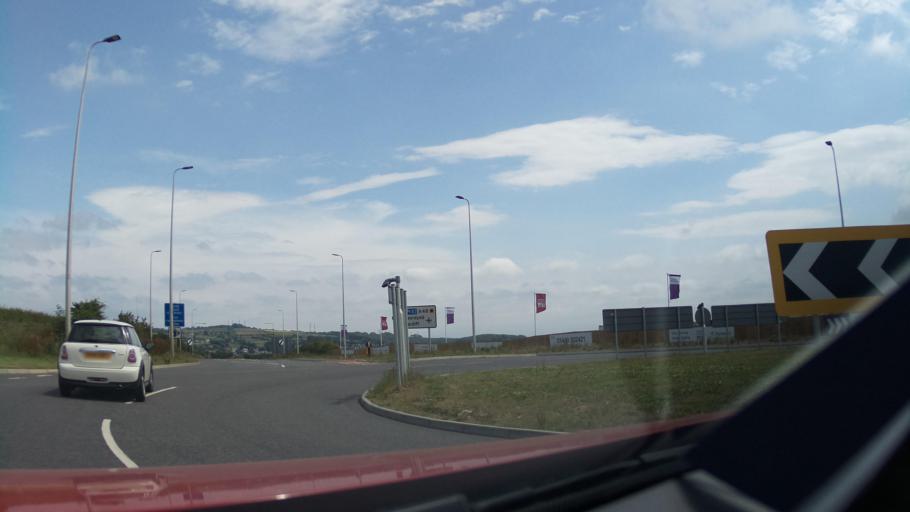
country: GB
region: Wales
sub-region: Vale of Glamorgan
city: Penllyn
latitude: 51.4668
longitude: -3.4681
